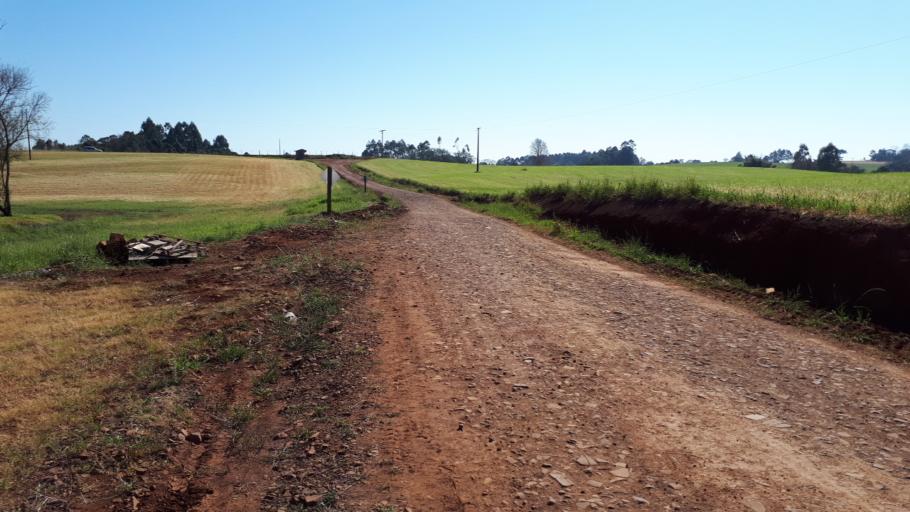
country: AR
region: Misiones
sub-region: Departamento de San Pedro
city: San Pedro
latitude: -26.8435
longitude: -53.6482
